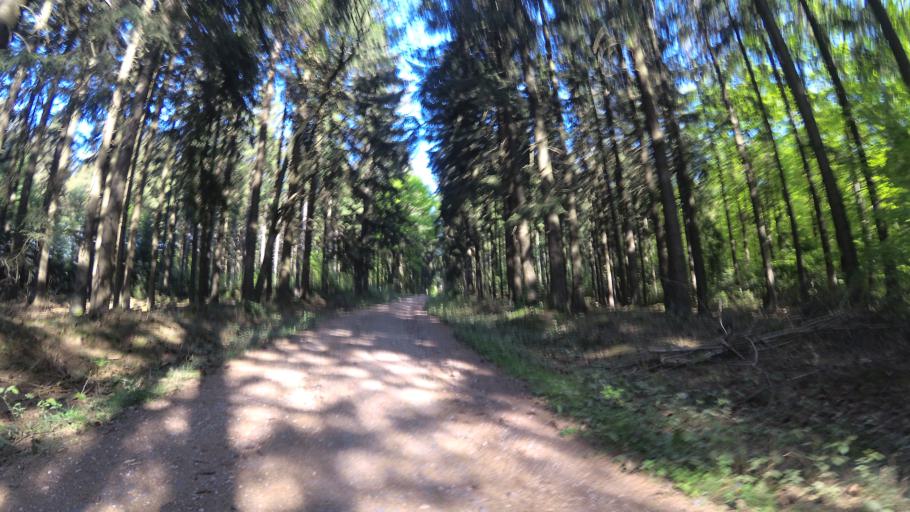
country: DE
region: Saarland
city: Mainzweiler
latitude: 49.4012
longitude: 7.1153
